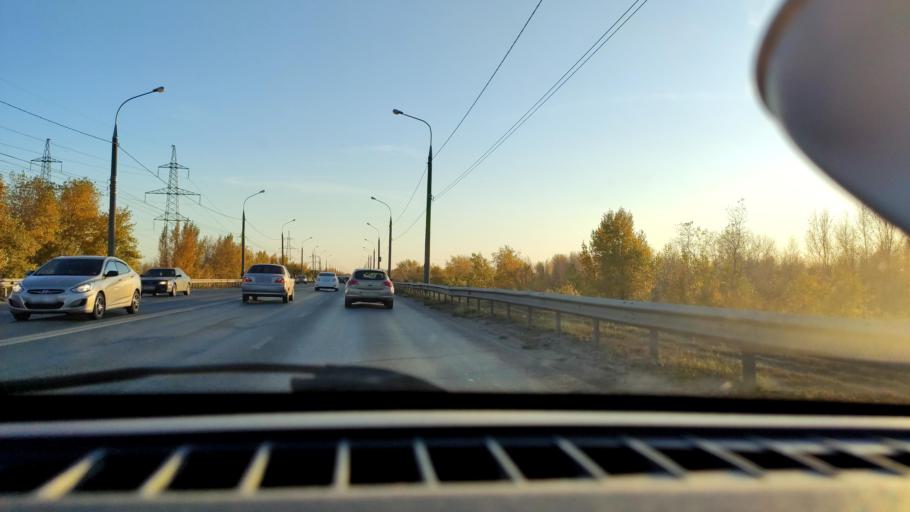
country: RU
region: Samara
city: Samara
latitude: 53.1629
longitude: 50.1939
